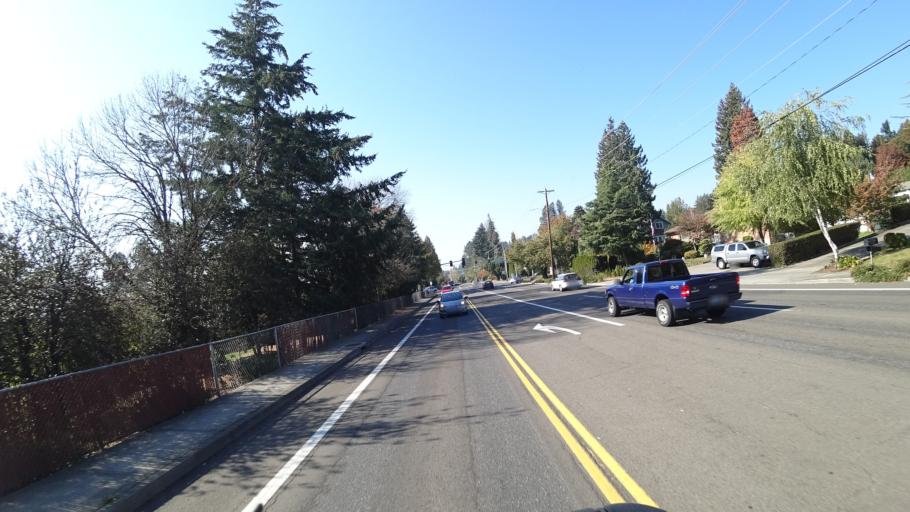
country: US
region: Oregon
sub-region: Multnomah County
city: Gresham
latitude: 45.4970
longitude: -122.4539
